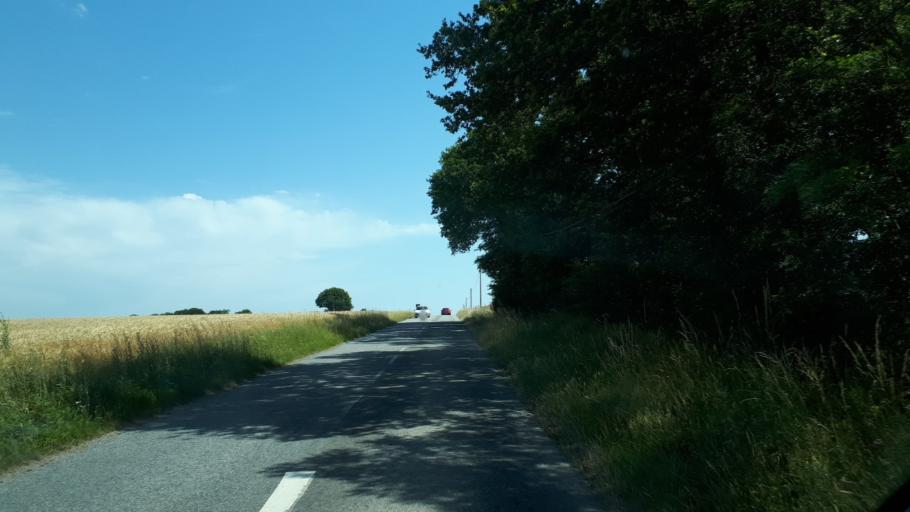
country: FR
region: Centre
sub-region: Departement d'Eure-et-Loir
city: Arrou
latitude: 48.0663
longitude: 1.1092
